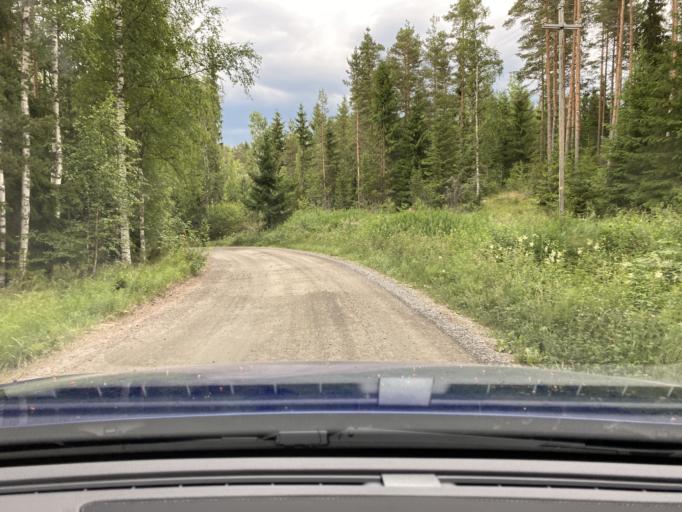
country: FI
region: Satakunta
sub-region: Rauma
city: Lappi
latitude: 61.1385
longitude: 21.9068
